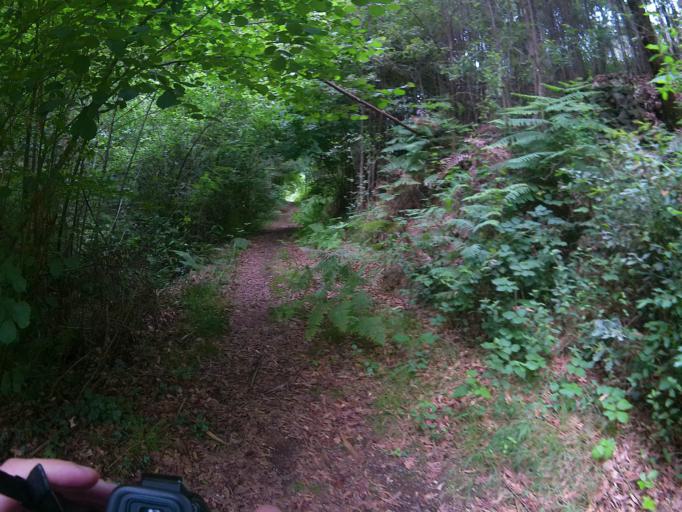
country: PT
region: Aveiro
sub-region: Albergaria-A-Velha
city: Branca
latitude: 40.7685
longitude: -8.4402
